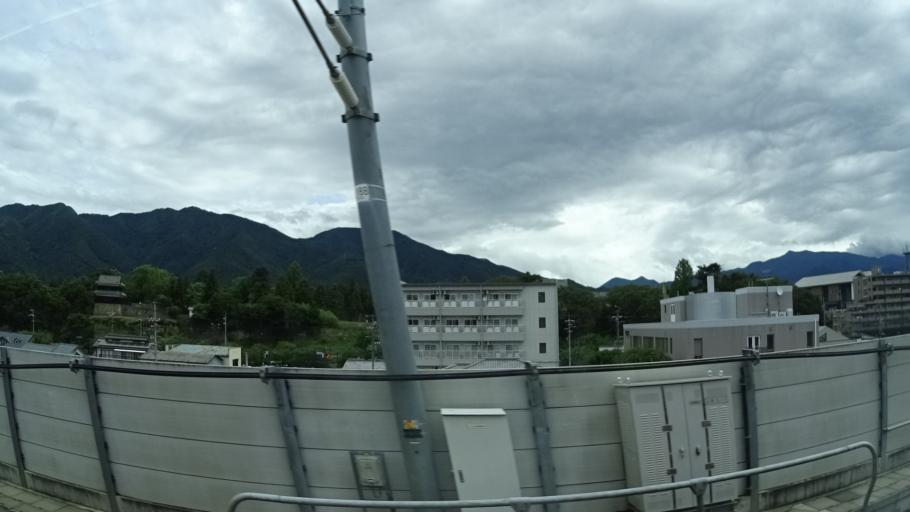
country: JP
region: Nagano
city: Ueda
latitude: 36.4058
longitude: 138.2352
